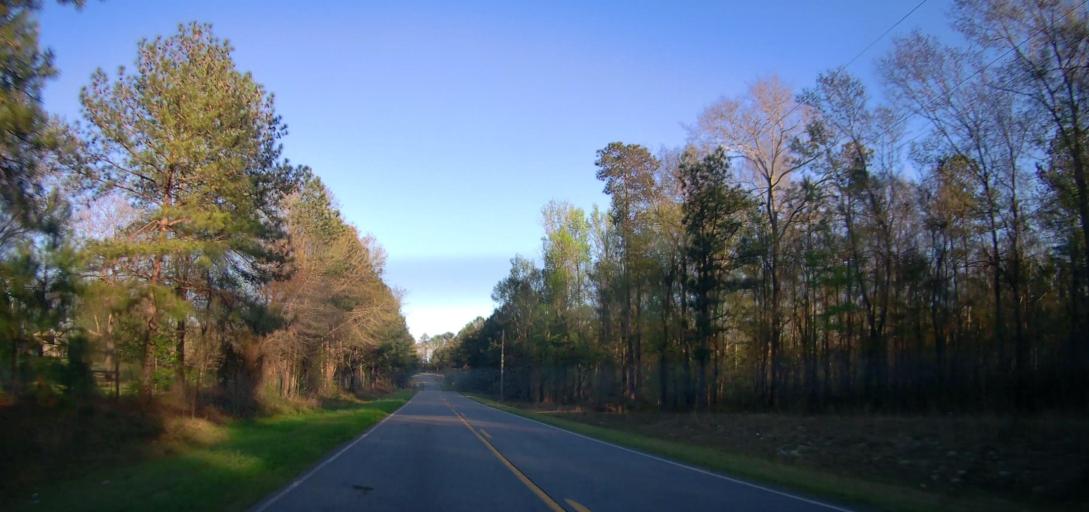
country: US
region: Georgia
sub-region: Wilkinson County
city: Gordon
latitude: 32.8795
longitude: -83.2748
